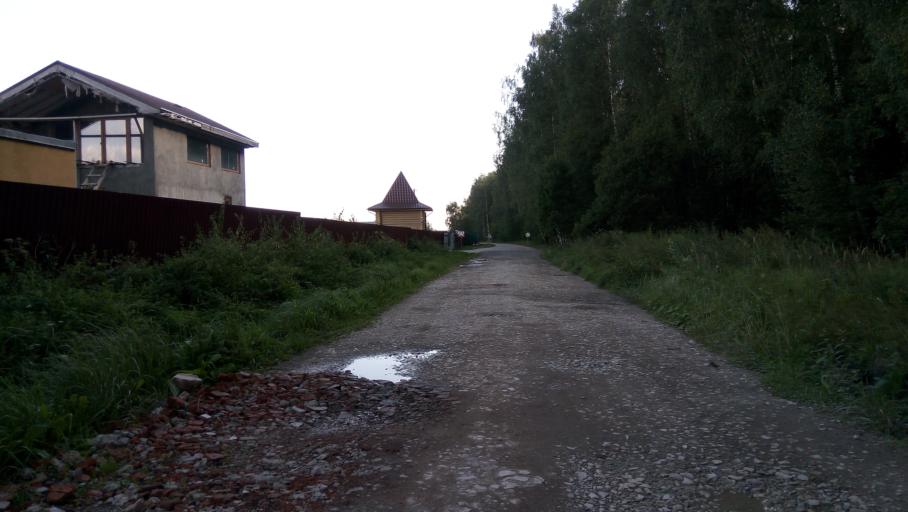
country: RU
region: Moskovskaya
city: Proletarskiy
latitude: 55.0501
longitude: 37.4008
